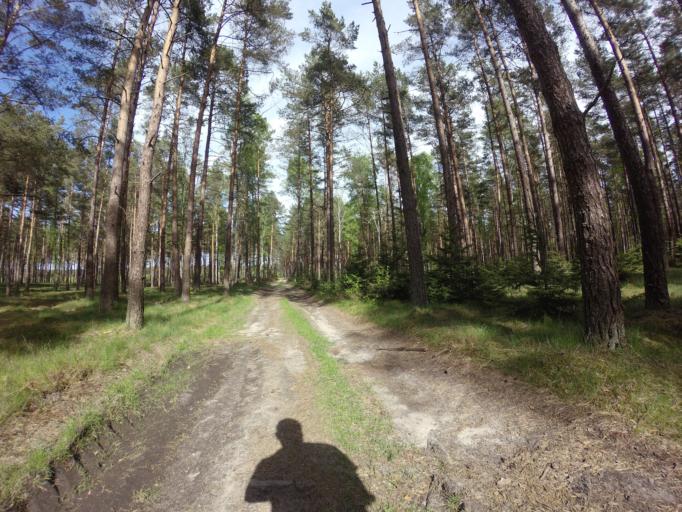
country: PL
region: West Pomeranian Voivodeship
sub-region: Powiat choszczenski
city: Drawno
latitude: 53.1951
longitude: 15.7336
